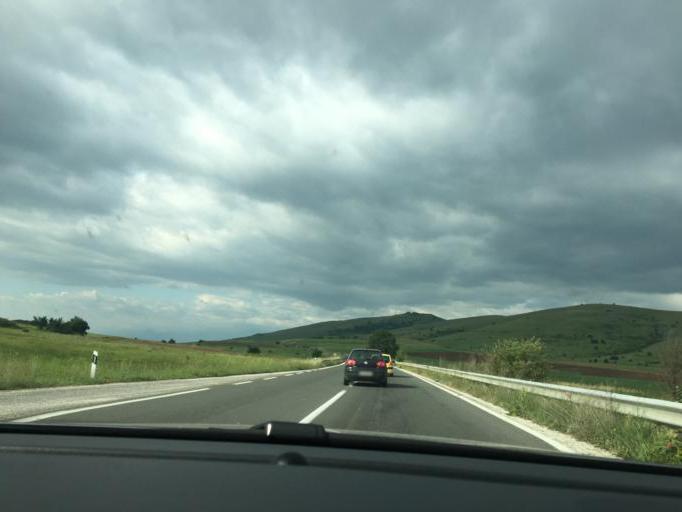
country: MK
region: Prilep
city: Topolcani
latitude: 41.2592
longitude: 21.4564
